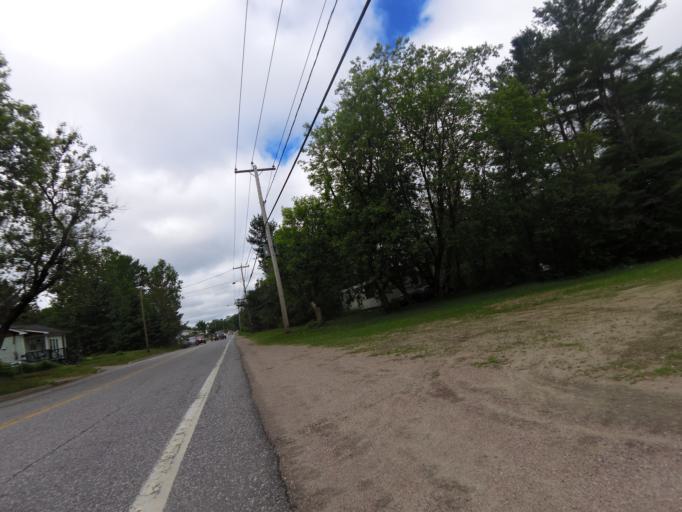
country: CA
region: Quebec
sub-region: Outaouais
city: Shawville
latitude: 45.8427
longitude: -76.4376
